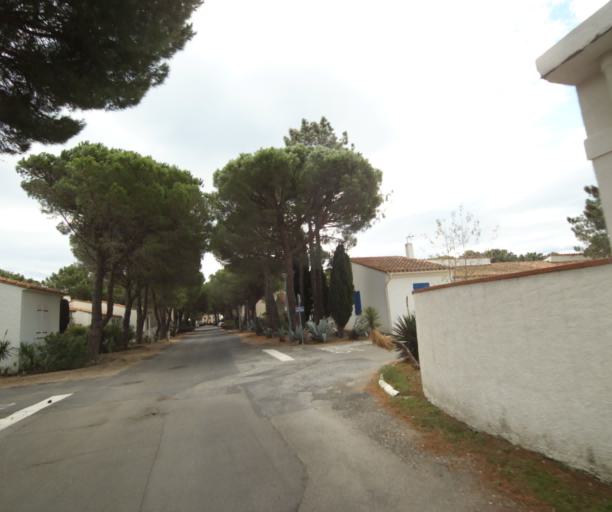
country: FR
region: Languedoc-Roussillon
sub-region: Departement des Pyrenees-Orientales
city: Argelers
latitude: 42.5632
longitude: 3.0426
